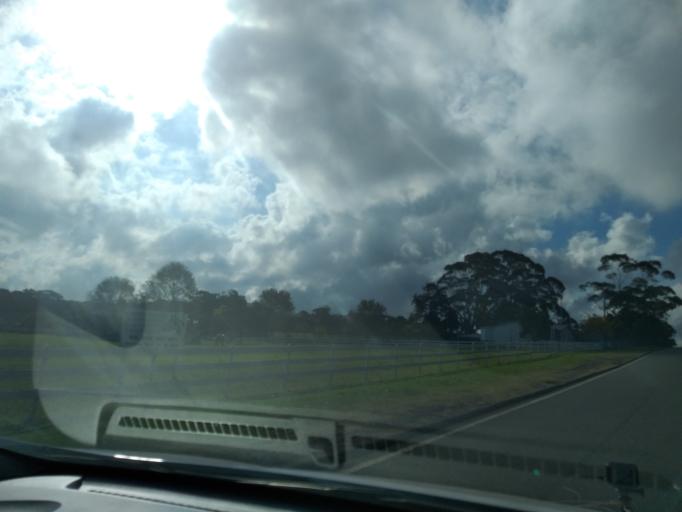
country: AU
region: New South Wales
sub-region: Wollongong
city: Helensburgh
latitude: -34.2044
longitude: 150.9793
